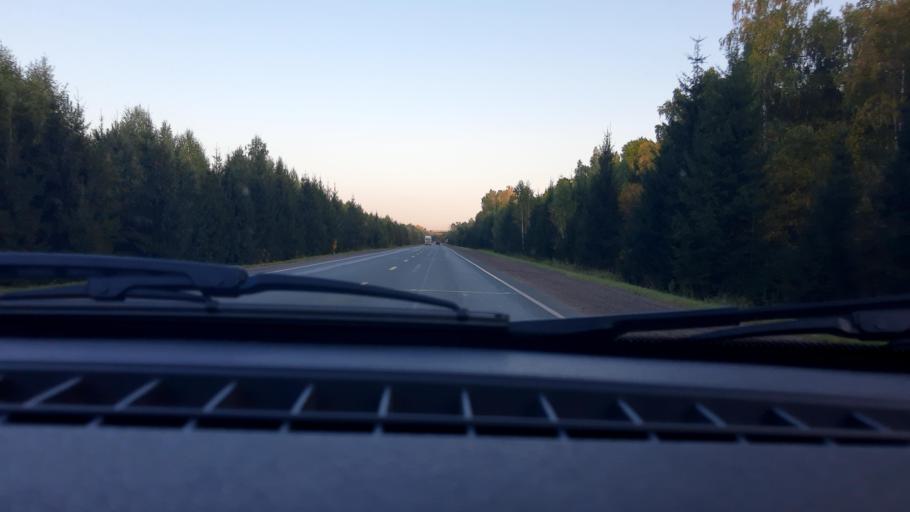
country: RU
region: Bashkortostan
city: Avdon
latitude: 54.8100
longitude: 55.7393
